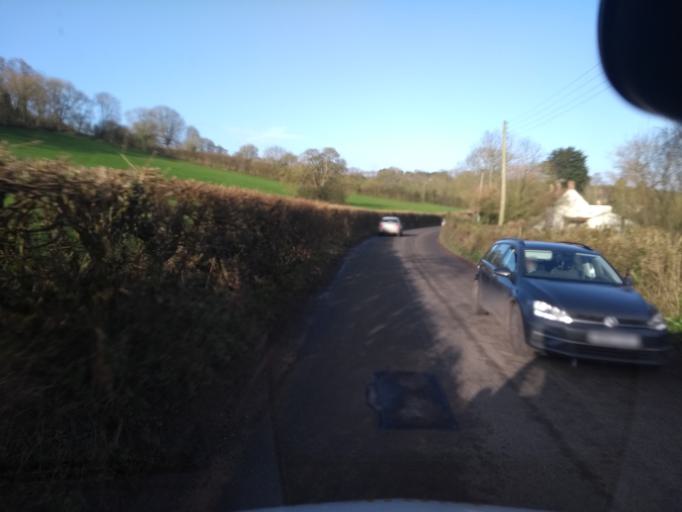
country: GB
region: England
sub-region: Somerset
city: Wedmore
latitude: 51.2132
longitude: -2.7786
